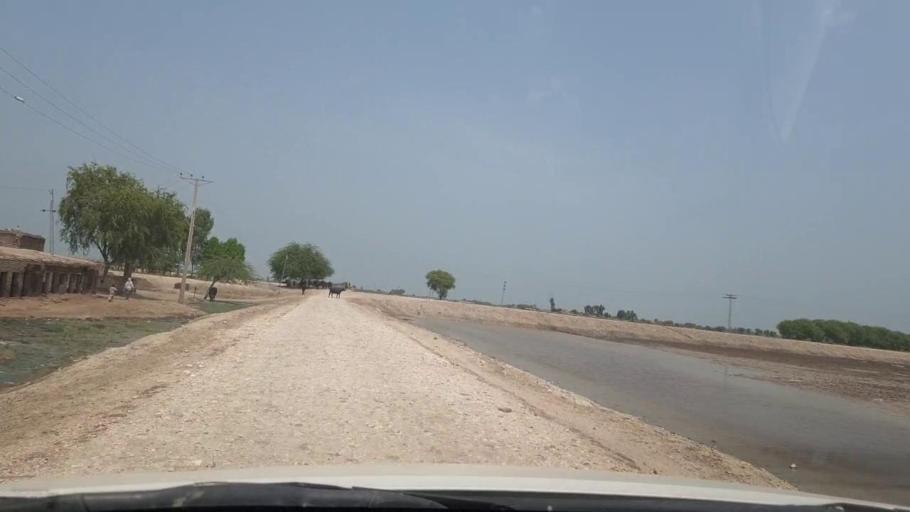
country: PK
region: Sindh
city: Rustam jo Goth
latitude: 28.0783
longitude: 68.8182
